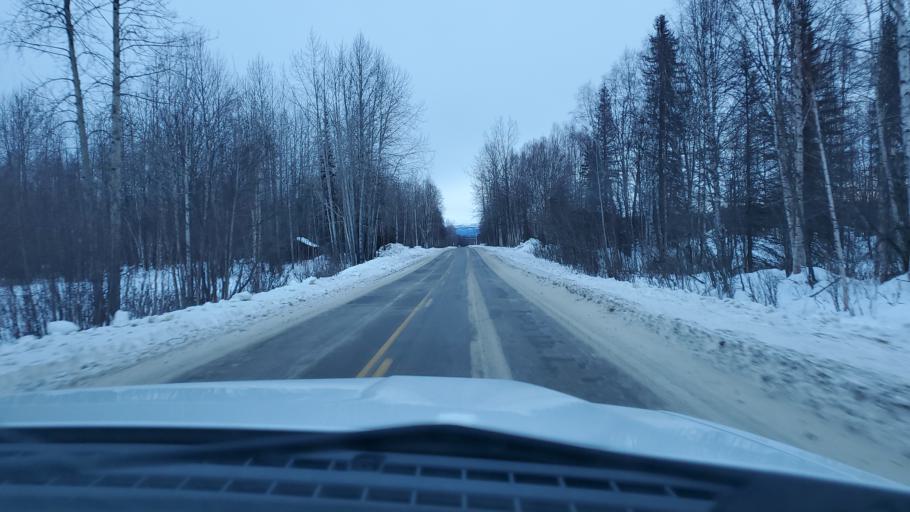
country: US
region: Alaska
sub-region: Matanuska-Susitna Borough
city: Y
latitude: 62.3163
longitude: -150.2441
